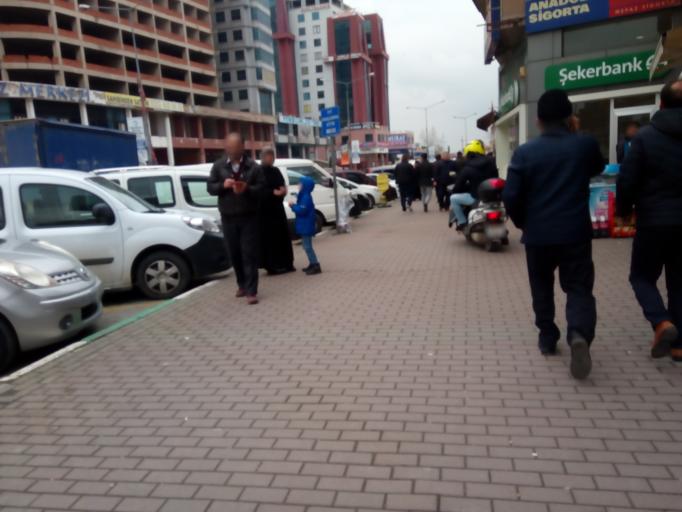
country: TR
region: Bursa
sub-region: Osmangazi
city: Bursa
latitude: 40.1890
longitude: 29.0621
